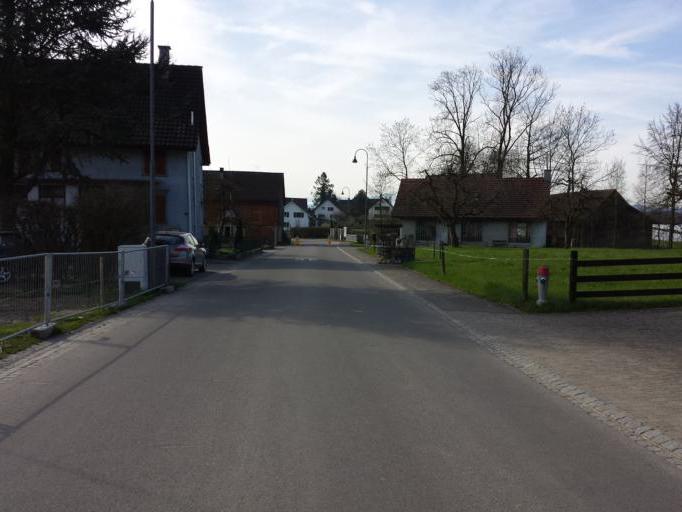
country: CH
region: Thurgau
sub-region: Arbon District
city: Salmsach
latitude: 47.5514
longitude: 9.3568
